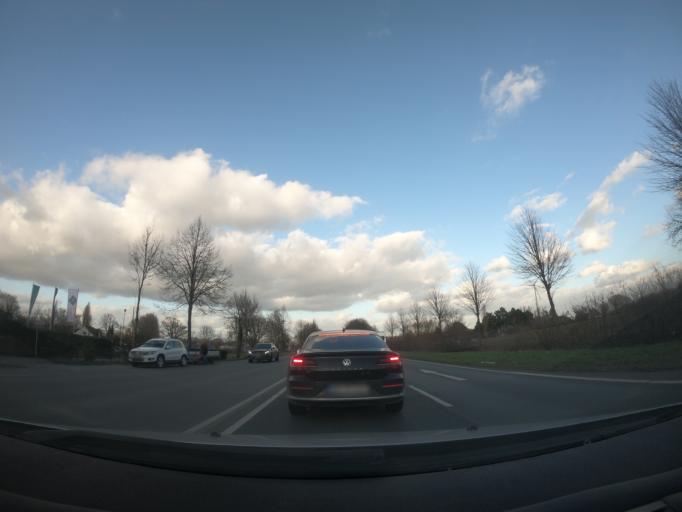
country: DE
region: North Rhine-Westphalia
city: Lunen
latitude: 51.5940
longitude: 7.4807
